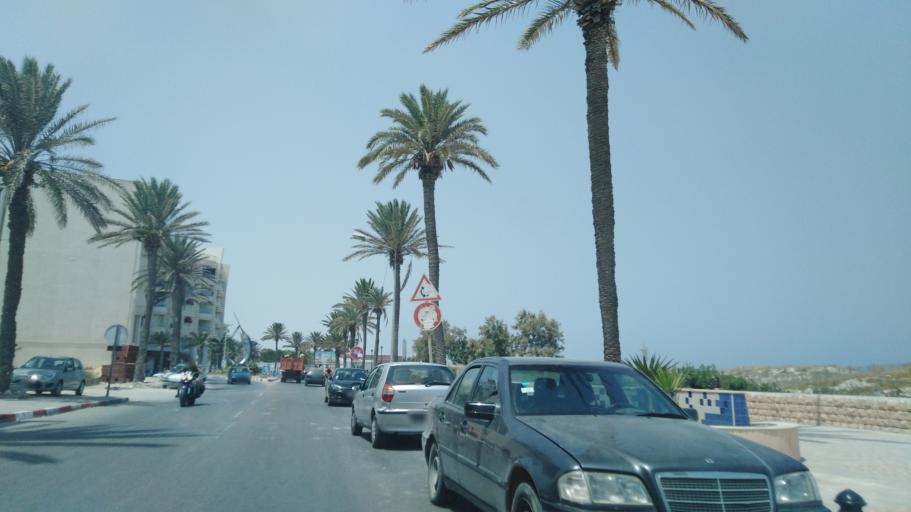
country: TN
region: Al Mahdiyah
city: Mahdia
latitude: 35.5105
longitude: 11.0535
